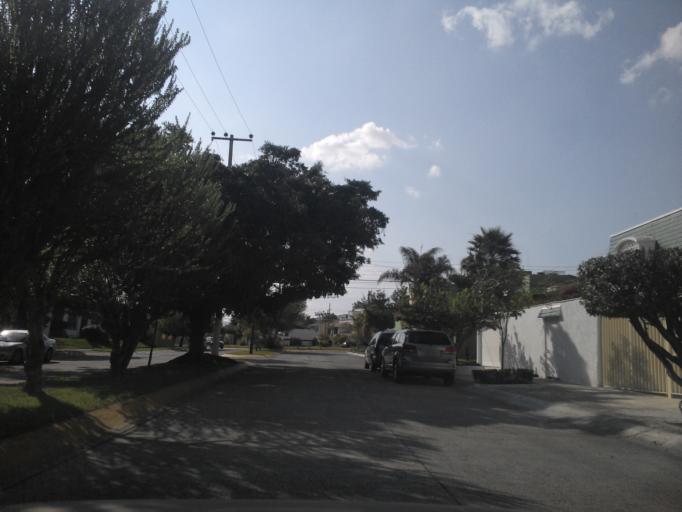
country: MX
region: Jalisco
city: Guadalajara
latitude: 20.6571
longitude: -103.4116
